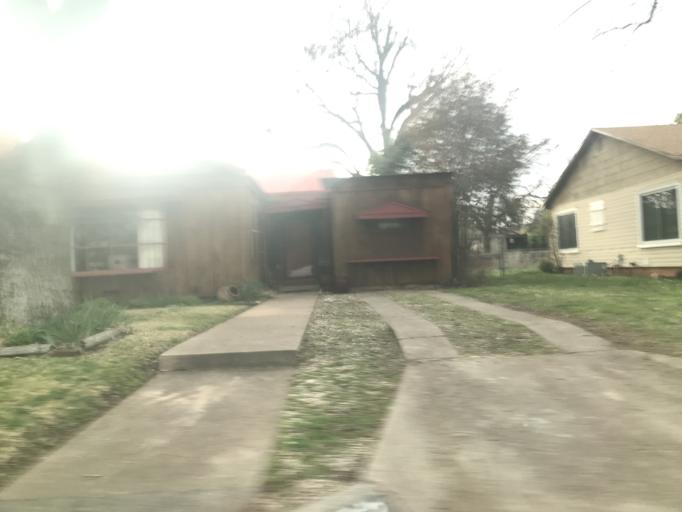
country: US
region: Texas
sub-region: Taylor County
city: Abilene
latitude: 32.4402
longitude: -99.7657
